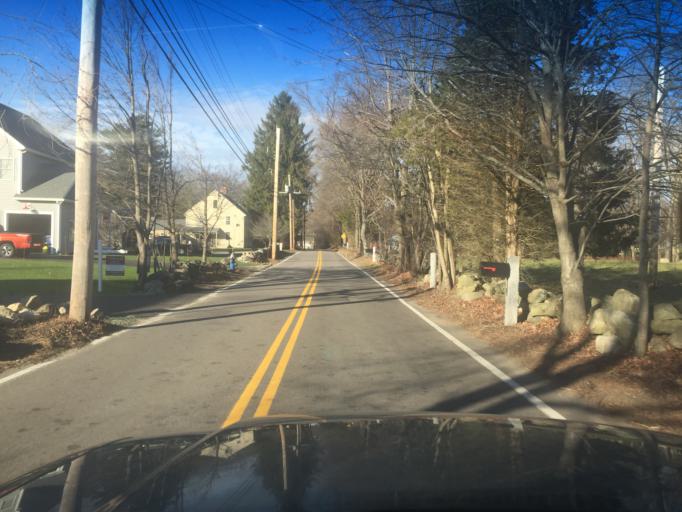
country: US
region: Massachusetts
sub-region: Norfolk County
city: Medway
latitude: 42.1613
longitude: -71.4210
